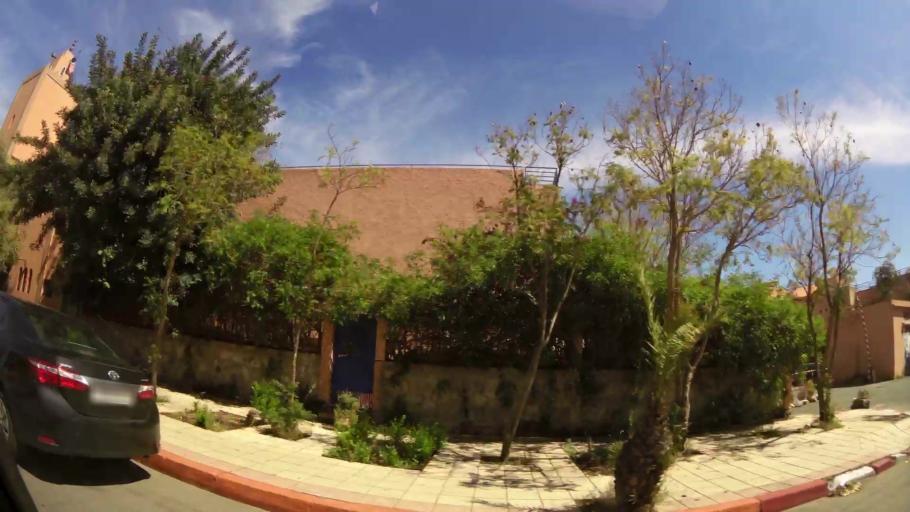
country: MA
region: Marrakech-Tensift-Al Haouz
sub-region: Marrakech
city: Marrakesh
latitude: 31.6683
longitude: -8.0082
